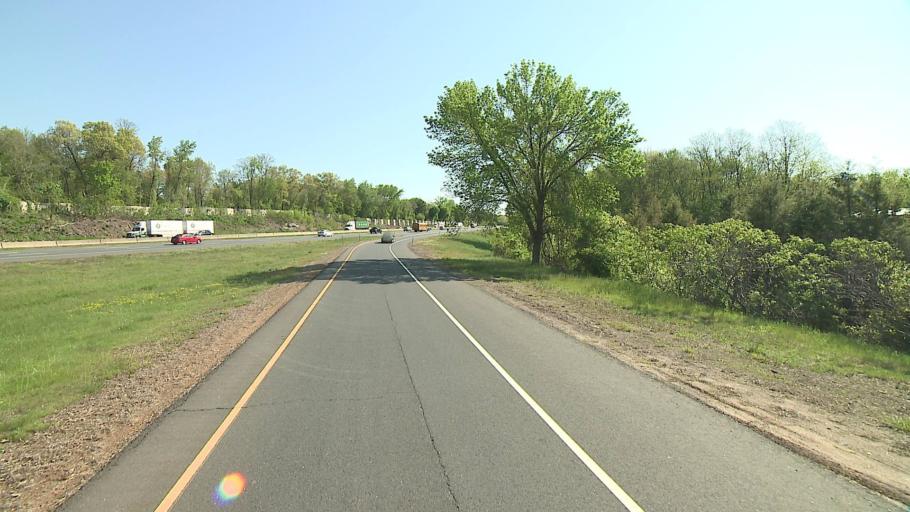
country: US
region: Connecticut
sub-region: Tolland County
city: Rockville
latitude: 41.8358
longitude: -72.4588
